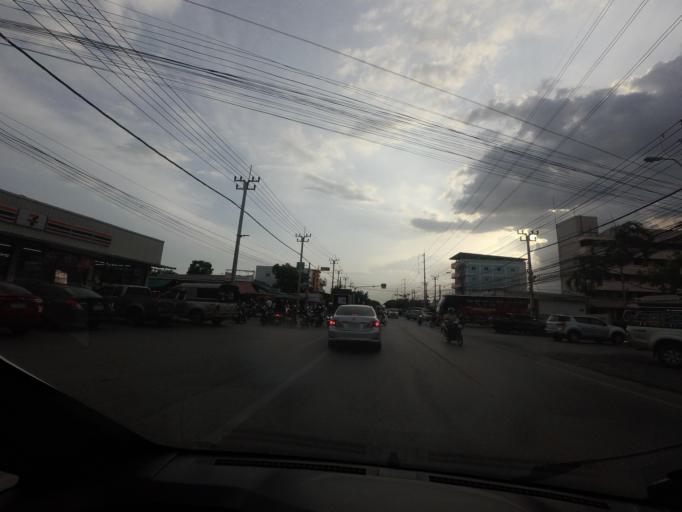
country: TH
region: Bangkok
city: Nong Chok
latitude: 13.8557
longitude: 100.8207
